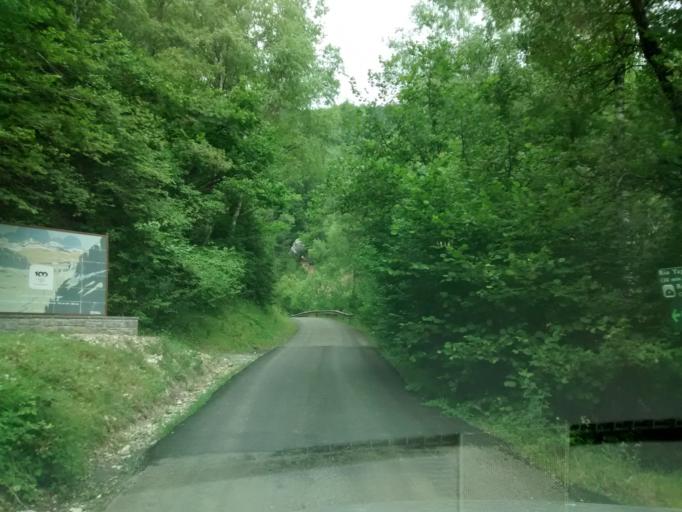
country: ES
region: Aragon
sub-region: Provincia de Huesca
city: Puertolas
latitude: 42.5905
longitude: 0.1271
